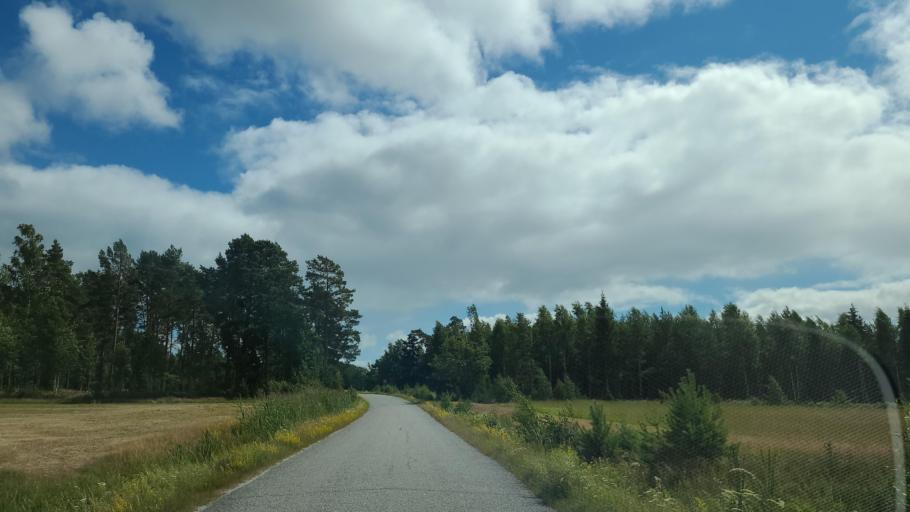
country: FI
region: Varsinais-Suomi
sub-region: Aboland-Turunmaa
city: Nagu
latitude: 60.1718
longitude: 22.0441
